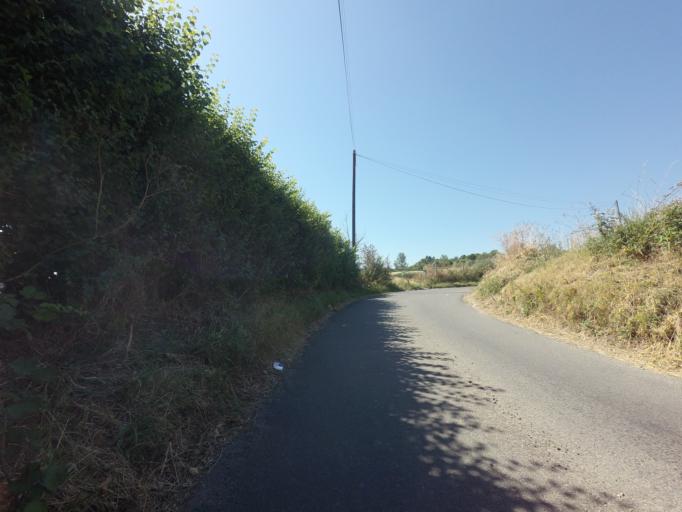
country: GB
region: England
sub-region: Kent
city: Swanley
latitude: 51.4098
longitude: 0.2059
